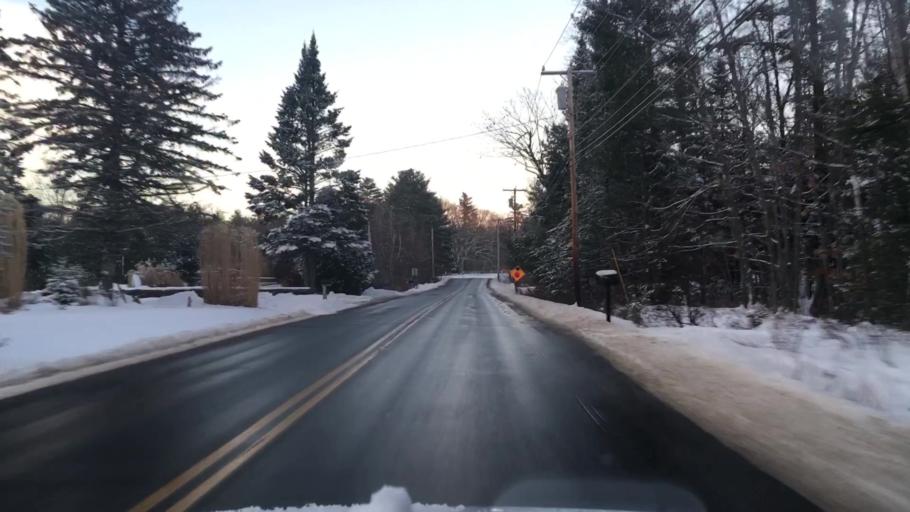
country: US
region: Maine
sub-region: Cumberland County
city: Brunswick
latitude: 43.9485
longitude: -69.9288
